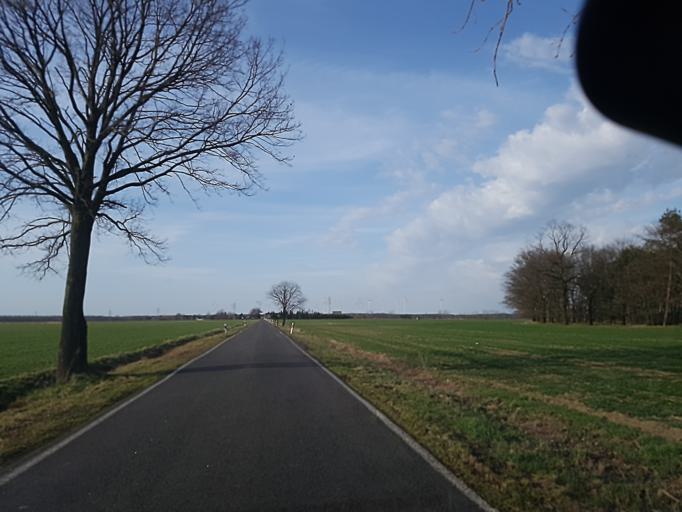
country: DE
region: Brandenburg
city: Falkenberg
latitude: 51.5362
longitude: 13.2951
